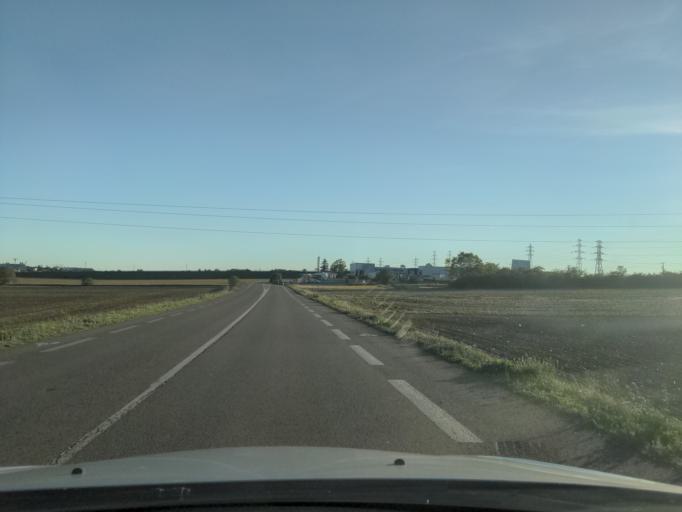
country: FR
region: Bourgogne
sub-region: Departement de la Cote-d'Or
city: Ruffey-les-Echirey
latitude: 47.3612
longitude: 5.0681
